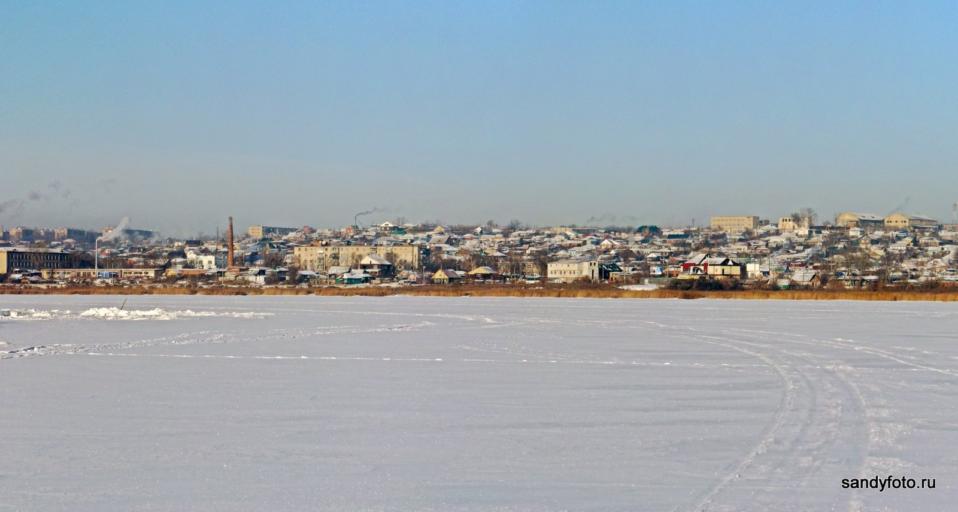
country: RU
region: Chelyabinsk
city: Troitsk
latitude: 54.0855
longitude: 61.5861
